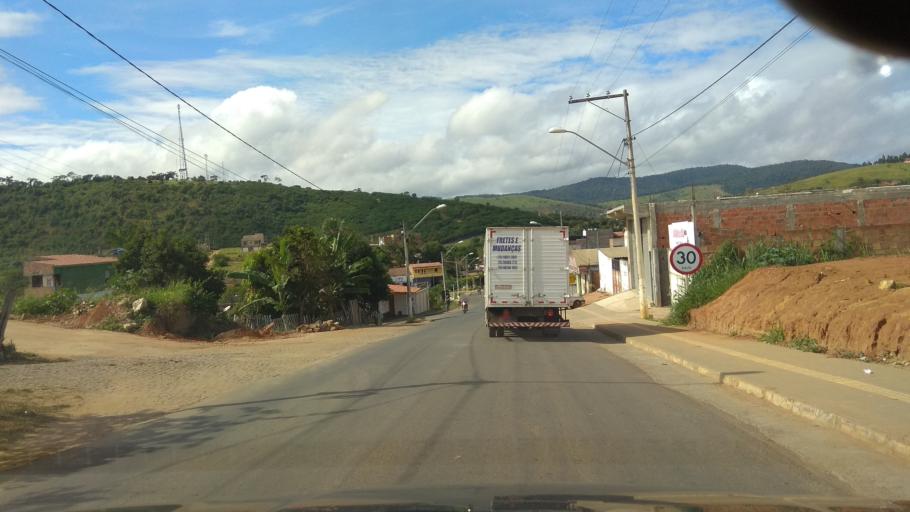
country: BR
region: Bahia
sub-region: Ubaira
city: Ubaira
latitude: -13.2622
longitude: -39.6635
